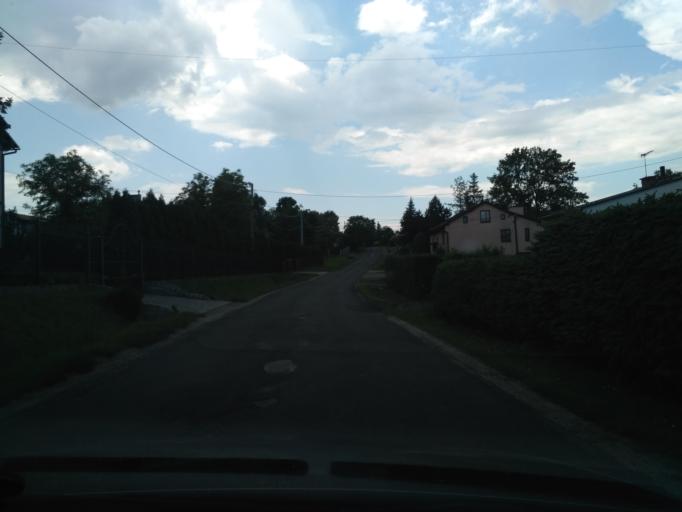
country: PL
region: Subcarpathian Voivodeship
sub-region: Powiat lancucki
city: Wysoka
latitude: 50.0406
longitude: 22.2474
